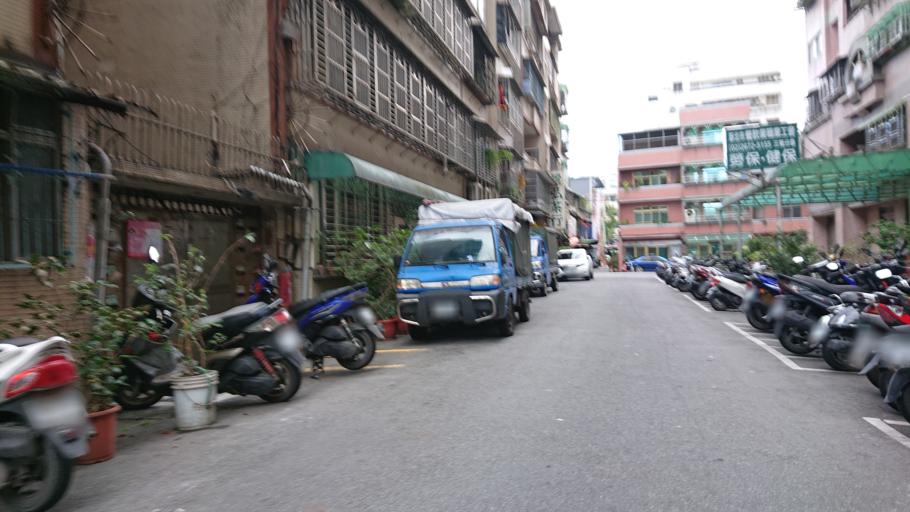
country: TW
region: Taiwan
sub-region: Taoyuan
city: Taoyuan
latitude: 24.9303
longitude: 121.3734
